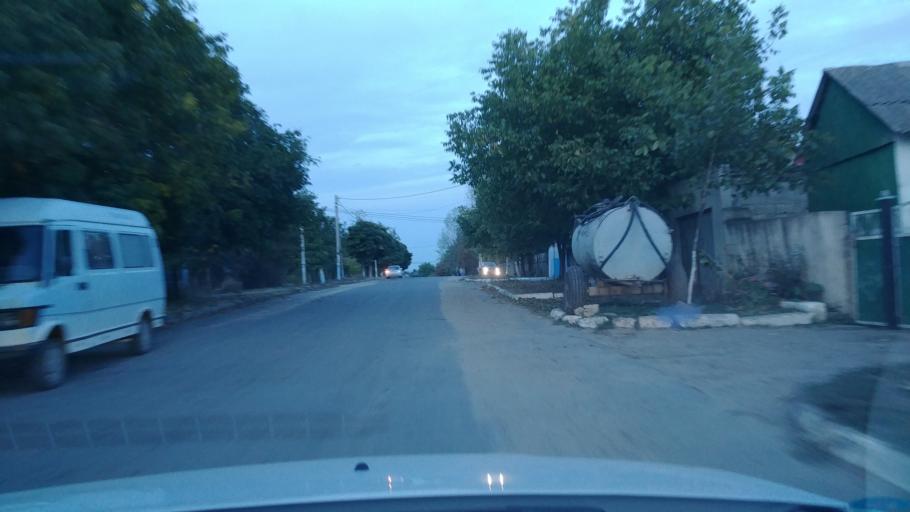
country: MD
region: Rezina
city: Saharna
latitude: 47.6728
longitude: 28.9541
